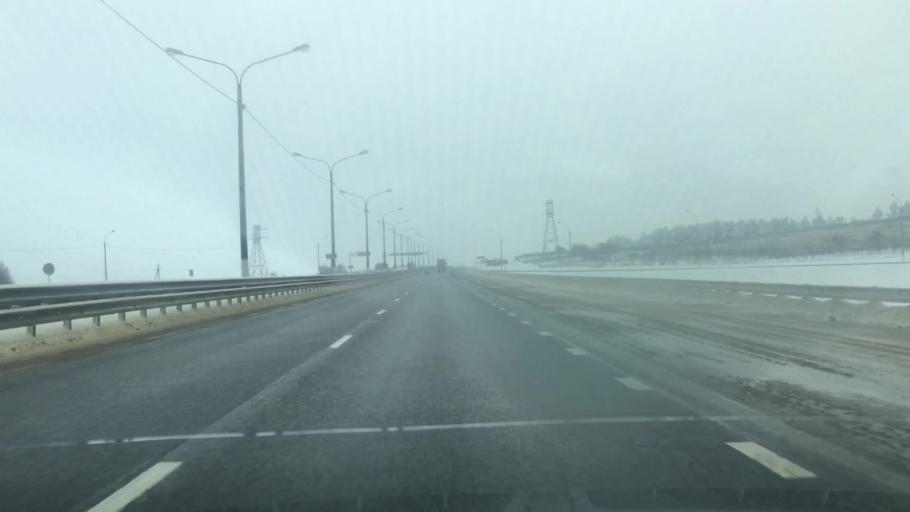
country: RU
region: Tula
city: Yefremov
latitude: 53.1622
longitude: 38.2487
